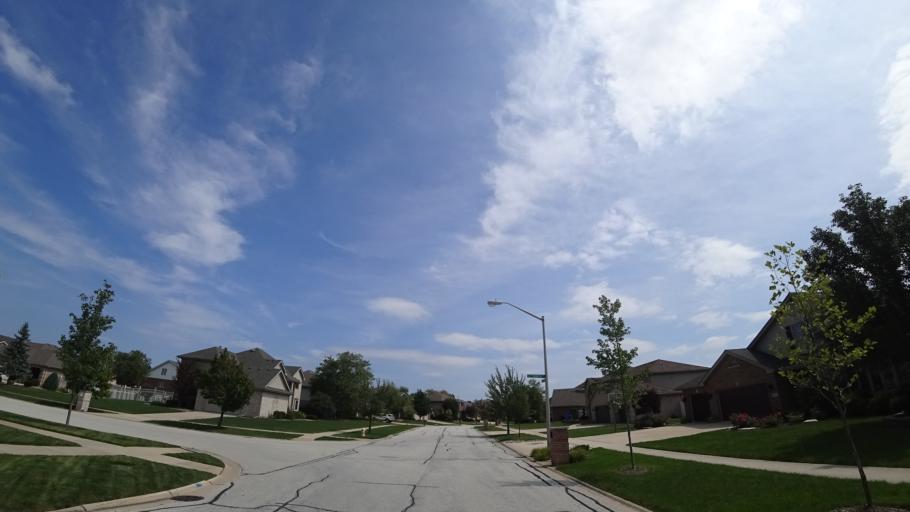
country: US
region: Illinois
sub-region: Cook County
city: Orland Hills
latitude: 41.5564
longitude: -87.8383
